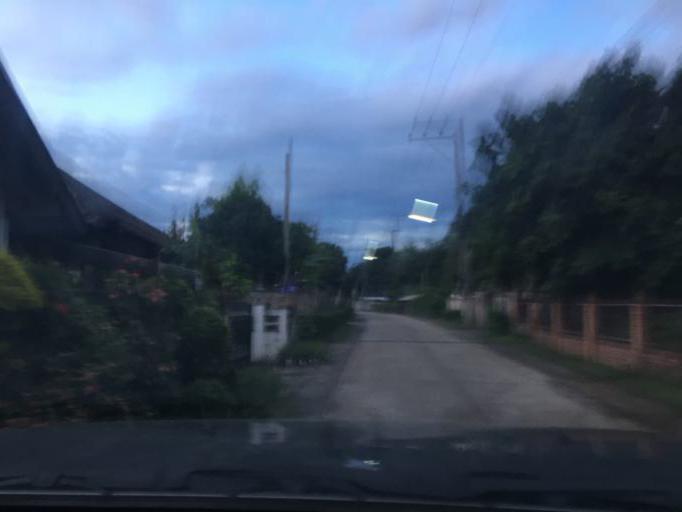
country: TH
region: Chiang Mai
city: San Sai
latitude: 18.8762
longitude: 98.9696
